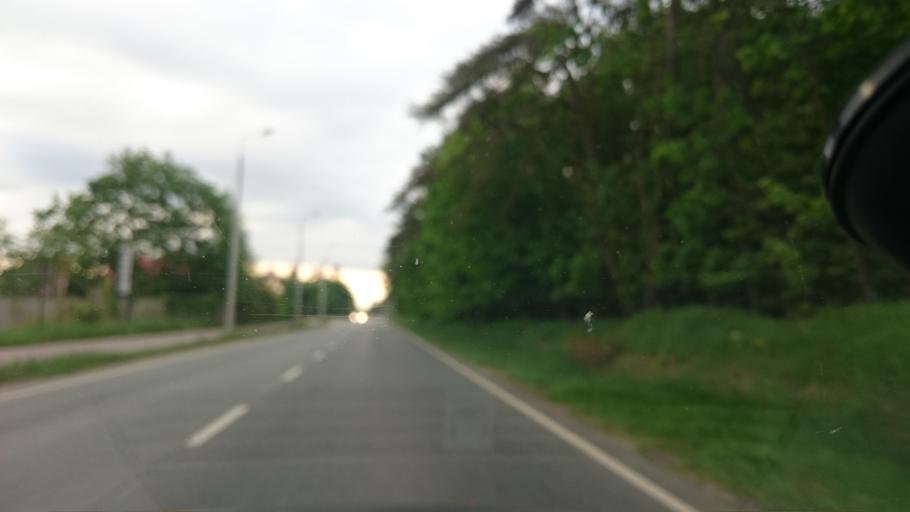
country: PL
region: Kujawsko-Pomorskie
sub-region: Grudziadz
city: Grudziadz
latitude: 53.4480
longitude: 18.8096
